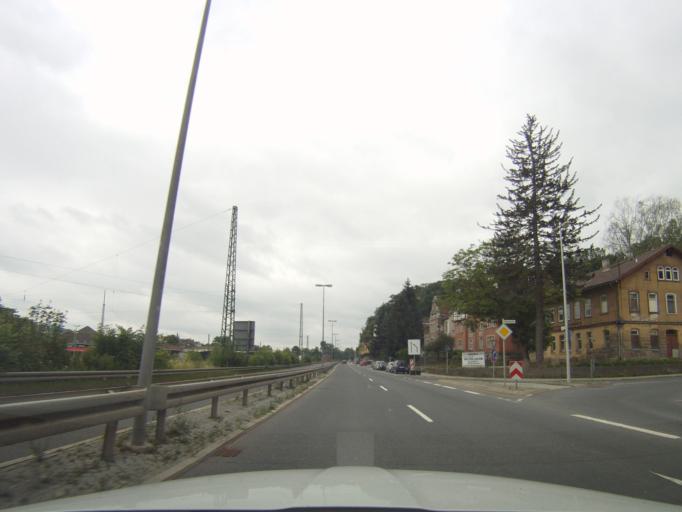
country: DE
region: Bavaria
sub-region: Upper Franconia
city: Coburg
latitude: 50.2642
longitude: 10.9560
